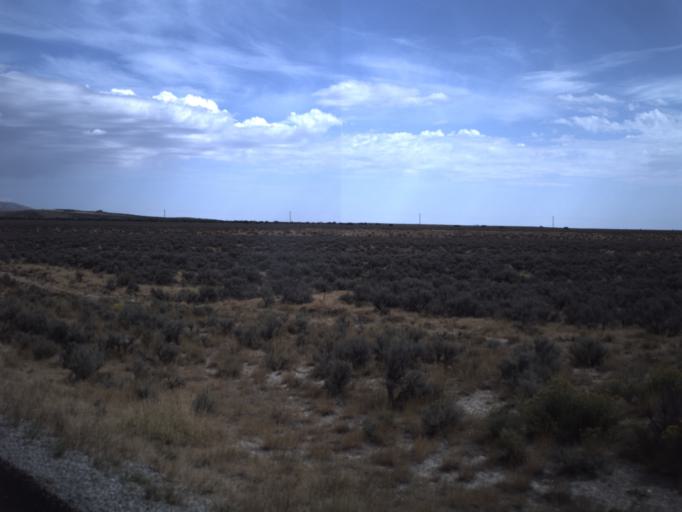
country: US
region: Idaho
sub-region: Cassia County
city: Burley
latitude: 41.7917
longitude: -113.4705
